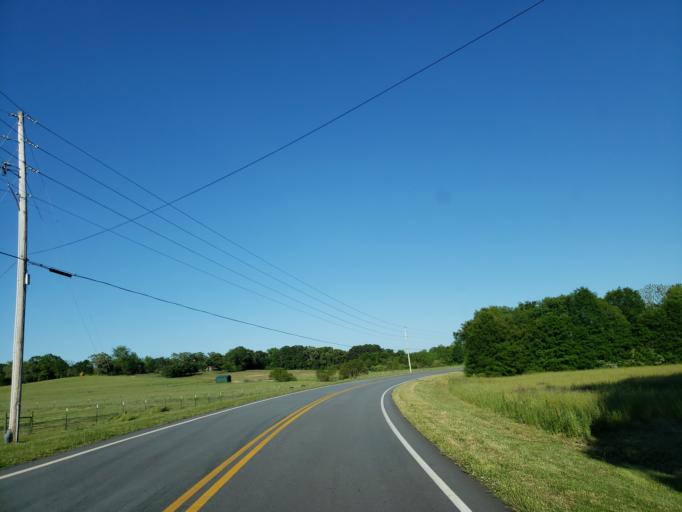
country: US
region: Georgia
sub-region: Haralson County
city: Tallapoosa
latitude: 33.7994
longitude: -85.2808
